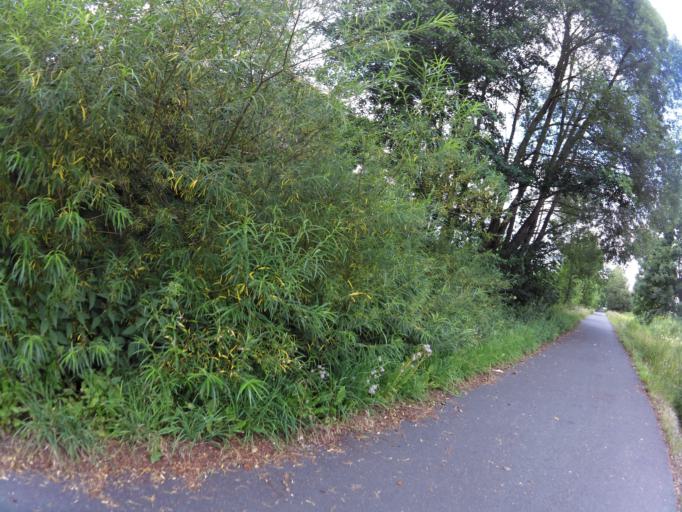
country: DE
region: Thuringia
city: Schleiz
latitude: 50.5791
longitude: 11.8028
